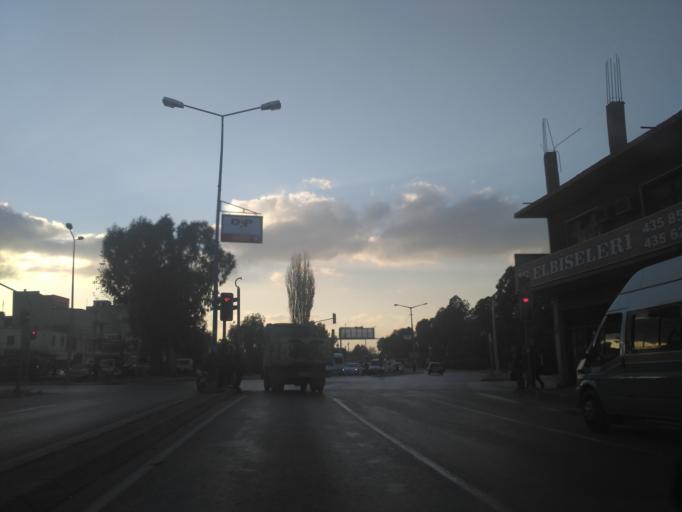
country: TR
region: Izmir
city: Buca
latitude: 38.4330
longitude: 27.1811
